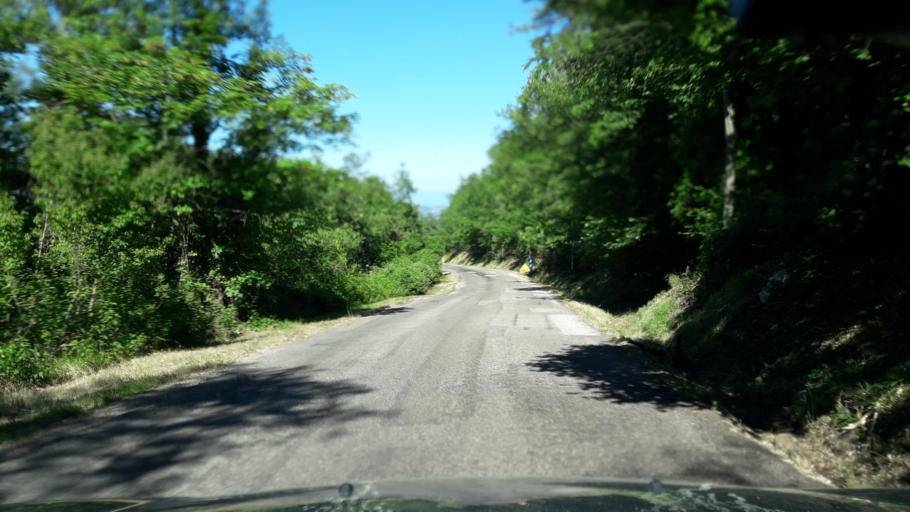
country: FR
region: Rhone-Alpes
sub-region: Departement de l'Ardeche
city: Privas
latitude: 44.7107
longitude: 4.5979
